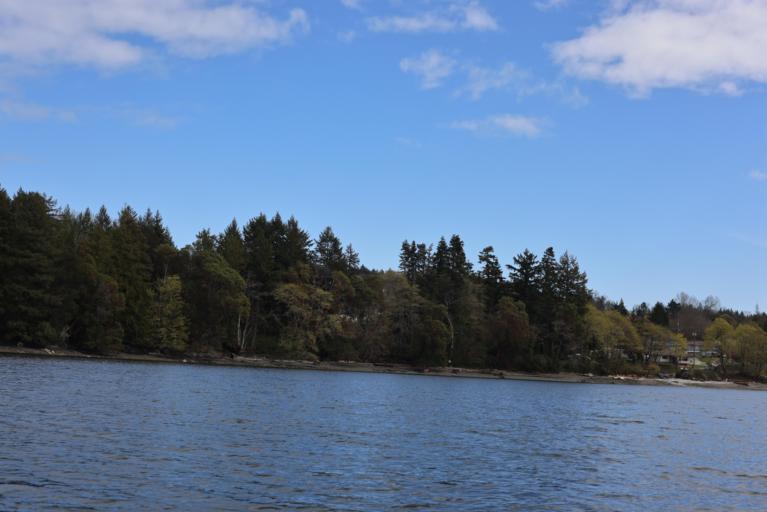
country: CA
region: British Columbia
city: North Saanich
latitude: 48.5863
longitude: -123.4700
